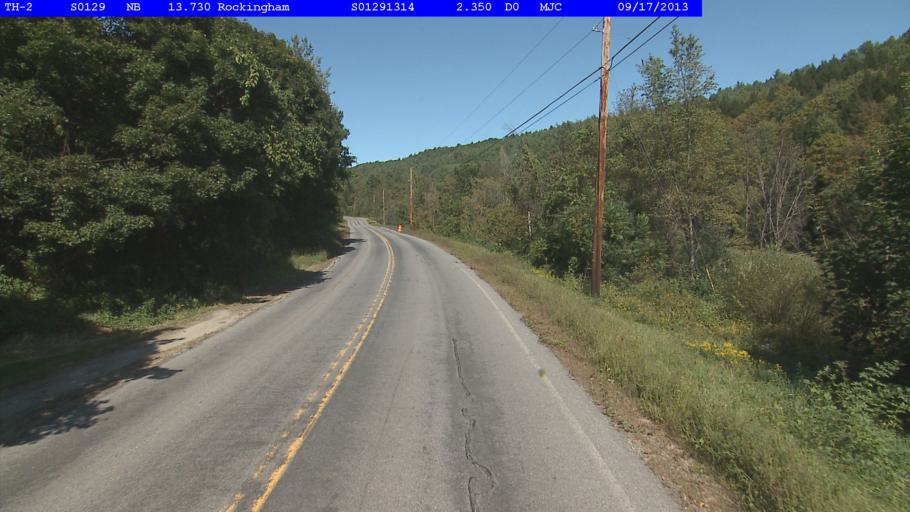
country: US
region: Vermont
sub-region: Windham County
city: Rockingham
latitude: 43.1513
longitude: -72.5182
